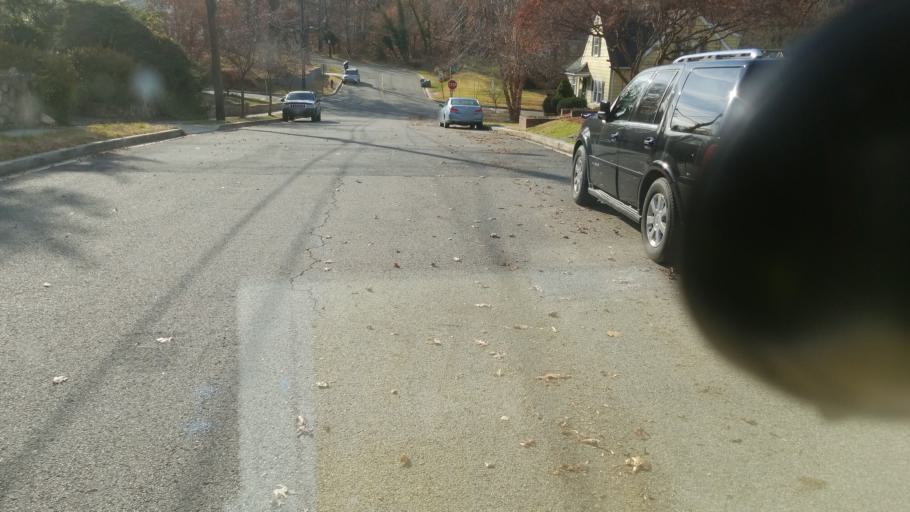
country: US
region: Maryland
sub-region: Prince George's County
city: Silver Hill
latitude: 38.8752
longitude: -76.9575
